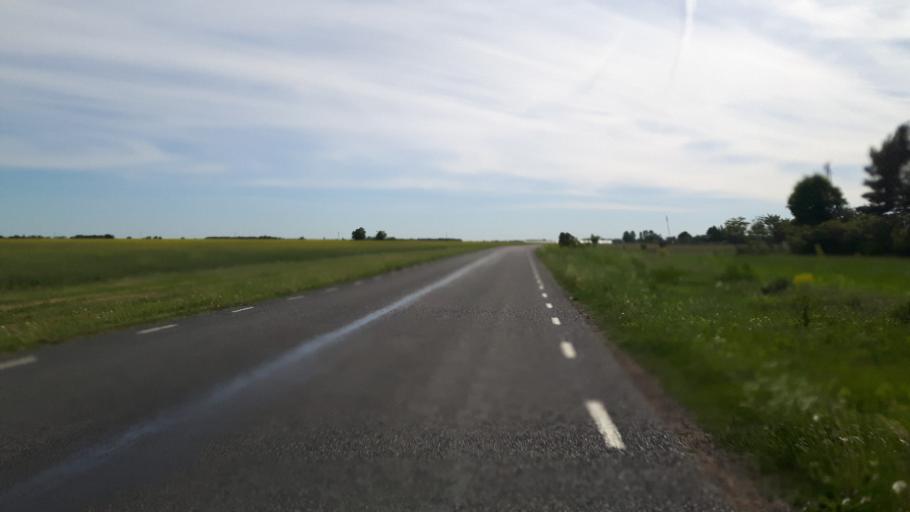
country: EE
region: Harju
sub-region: Raasiku vald
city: Arukula
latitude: 59.4371
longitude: 25.1266
